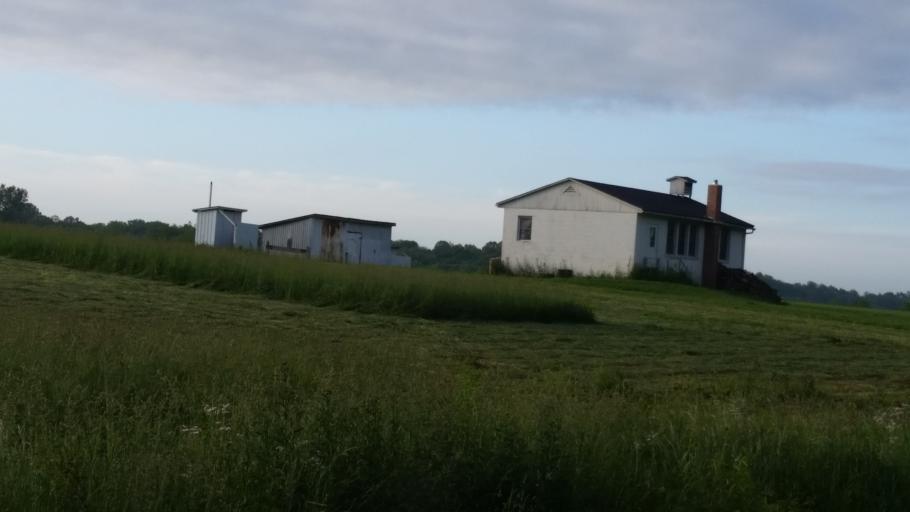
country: US
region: Ohio
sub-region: Sandusky County
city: Bellville
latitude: 40.5714
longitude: -82.6049
